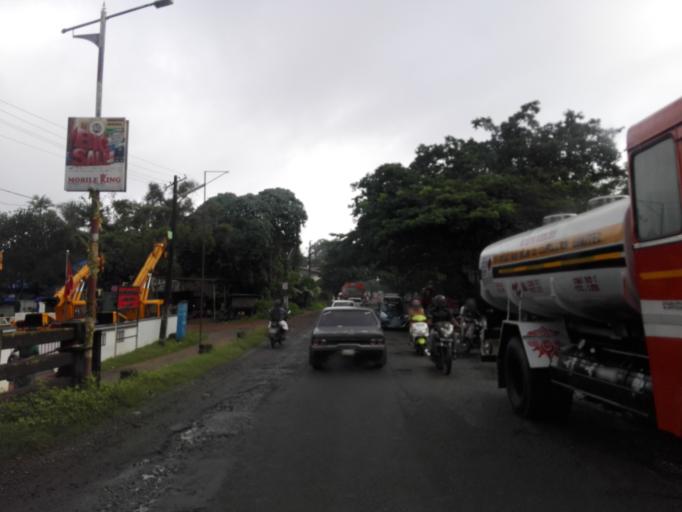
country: IN
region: Kerala
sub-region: Ernakulam
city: Cochin
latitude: 9.9744
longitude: 76.3549
